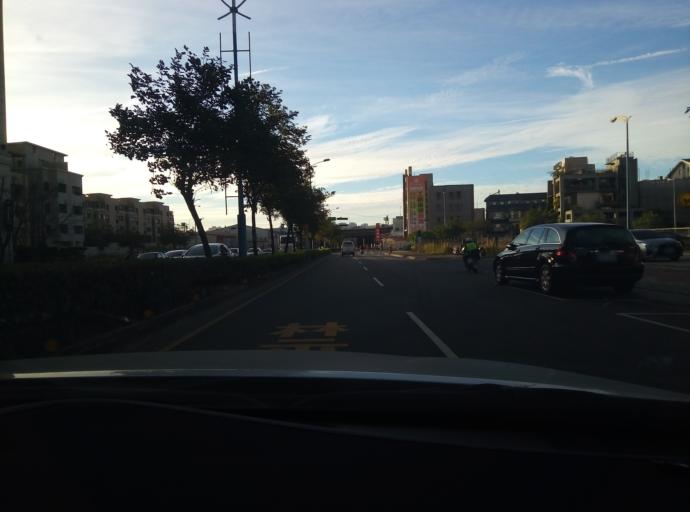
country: TW
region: Taiwan
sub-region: Taichung City
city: Taichung
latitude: 24.1852
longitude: 120.6396
